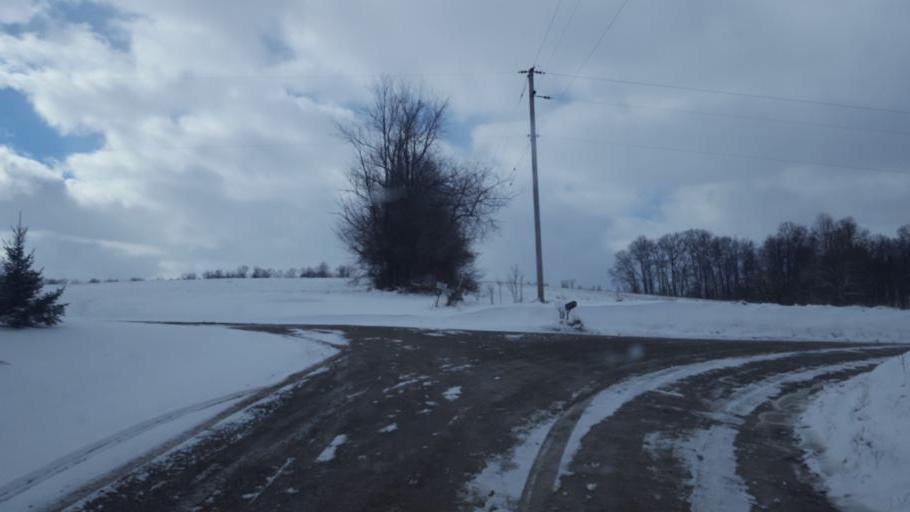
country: US
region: Ohio
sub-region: Knox County
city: Gambier
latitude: 40.5189
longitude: -82.3907
